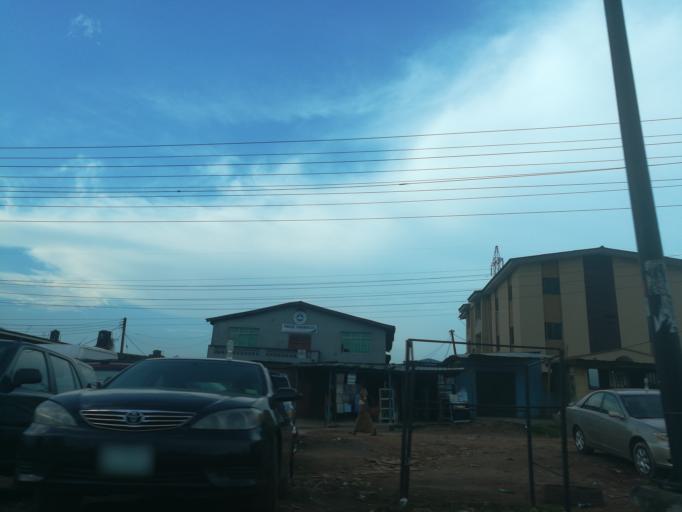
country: NG
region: Lagos
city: Ikorodu
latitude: 6.6251
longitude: 3.4906
